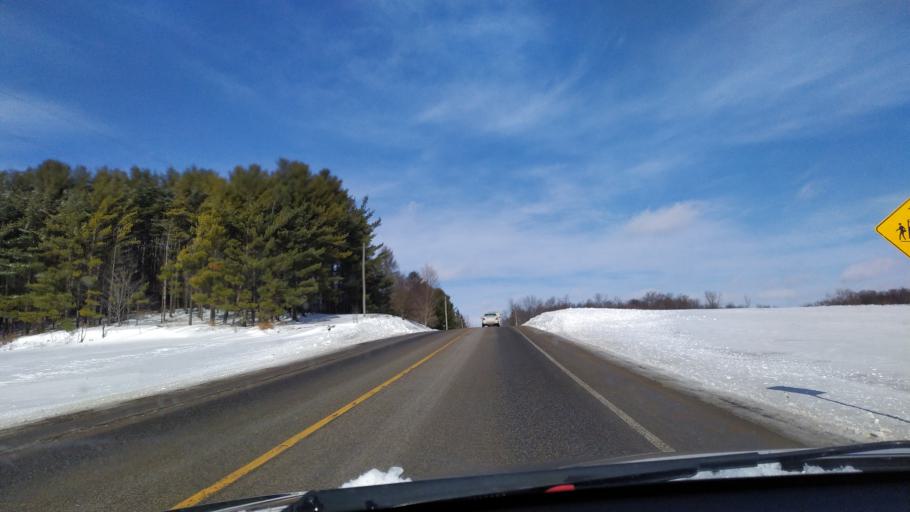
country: CA
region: Ontario
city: Waterloo
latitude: 43.5135
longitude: -80.6842
